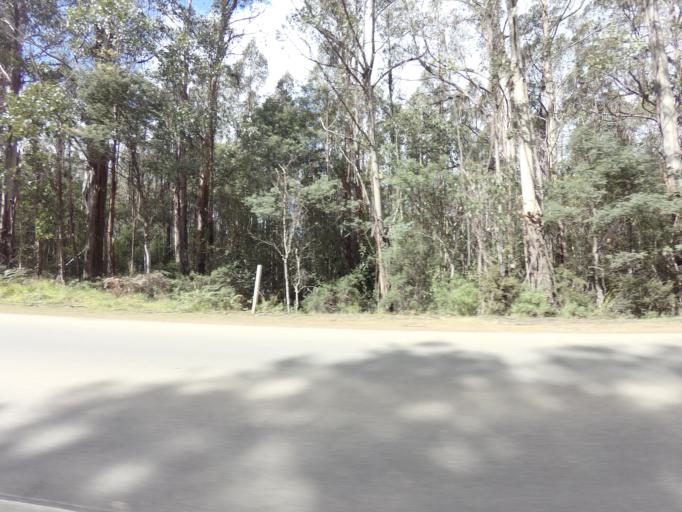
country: AU
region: Tasmania
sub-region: Huon Valley
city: Geeveston
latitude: -43.3470
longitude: 146.9618
